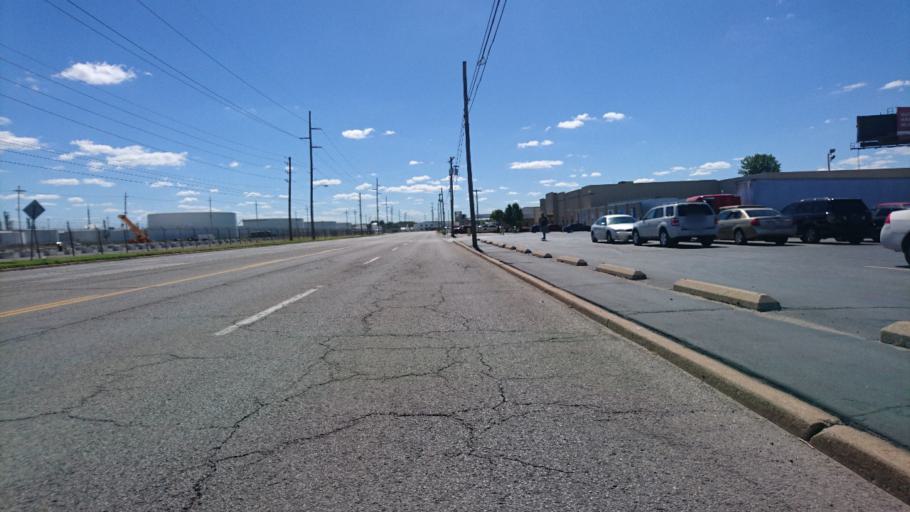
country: US
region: Oklahoma
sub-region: Tulsa County
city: Tulsa
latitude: 36.1208
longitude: -96.0073
